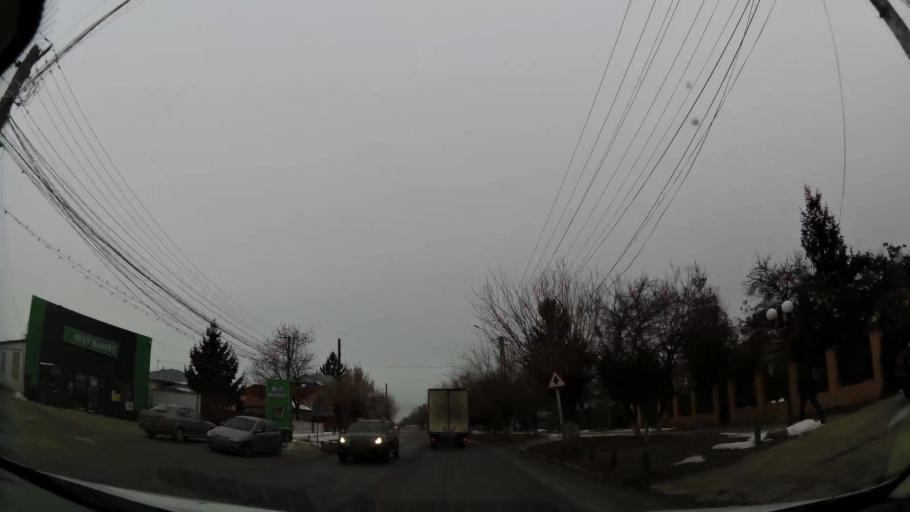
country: RO
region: Dambovita
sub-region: Comuna Racari
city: Racari
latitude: 44.6254
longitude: 25.7445
